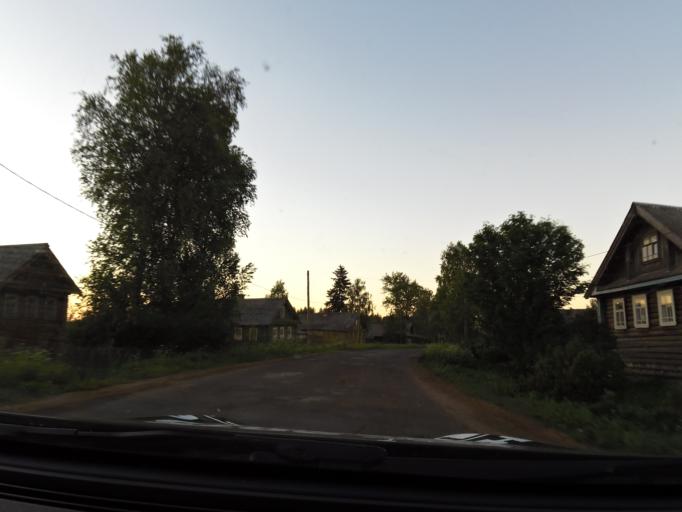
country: RU
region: Leningrad
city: Voznesen'ye
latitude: 60.8261
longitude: 35.7339
